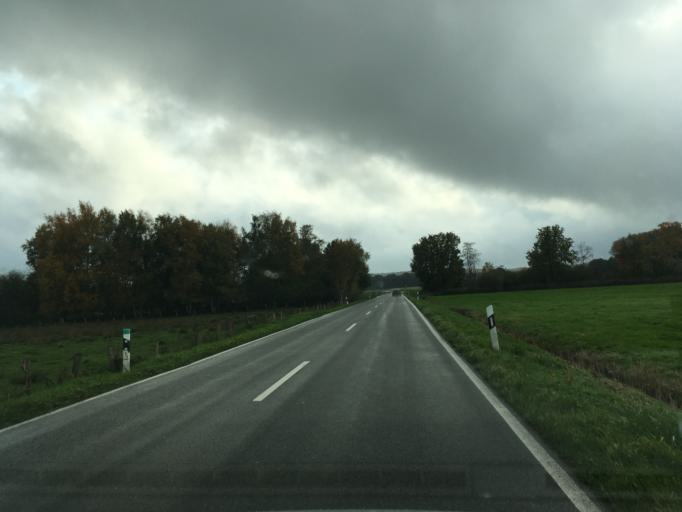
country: DE
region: North Rhine-Westphalia
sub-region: Regierungsbezirk Munster
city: Velen
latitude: 51.8614
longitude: 7.0337
